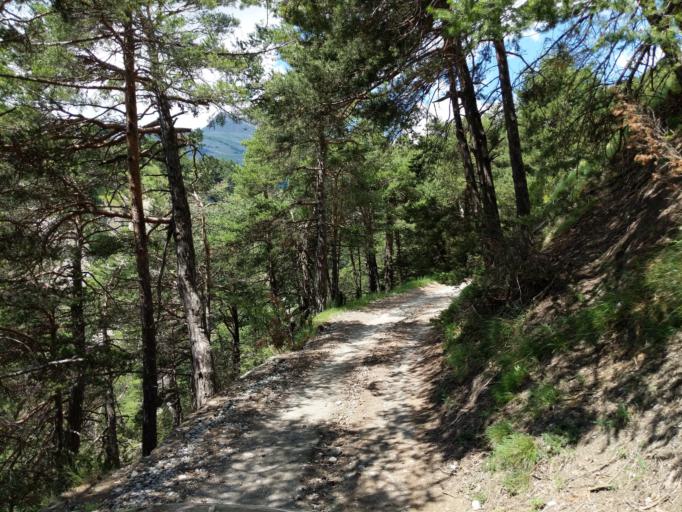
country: FR
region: Rhone-Alpes
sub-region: Departement de la Savoie
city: Modane
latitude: 45.2233
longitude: 6.7505
